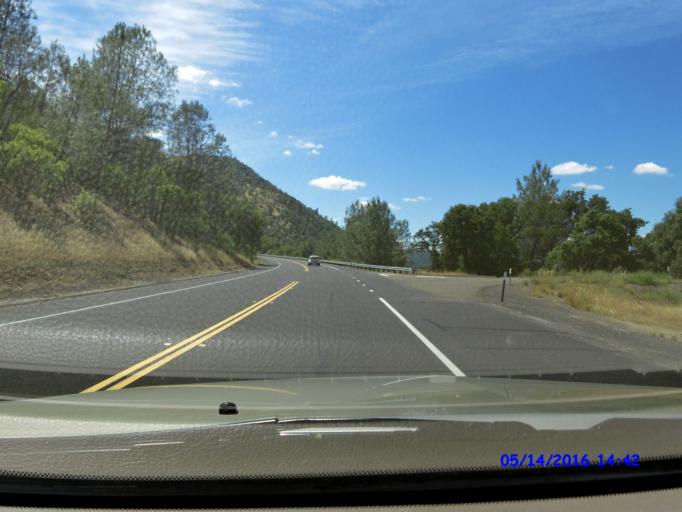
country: US
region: California
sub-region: Tuolumne County
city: Jamestown
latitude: 37.8306
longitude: -120.3481
